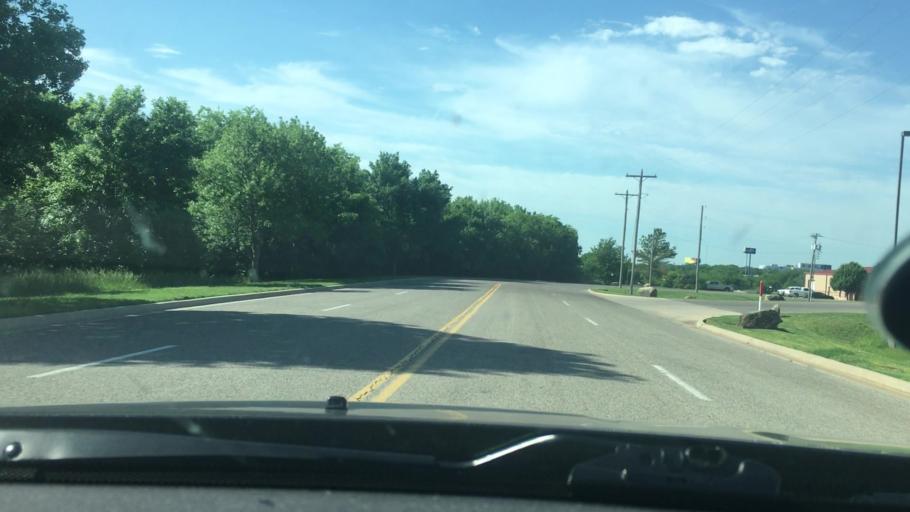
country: US
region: Oklahoma
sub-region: Carter County
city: Ardmore
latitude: 34.1949
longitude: -97.1673
